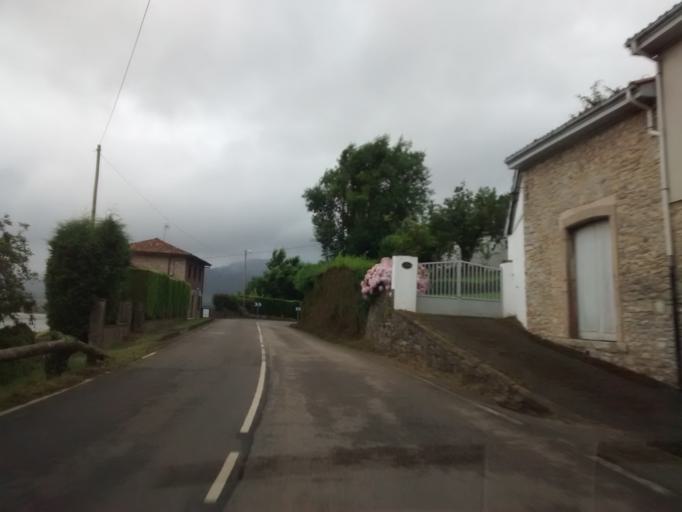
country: ES
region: Asturias
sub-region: Province of Asturias
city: Villaviciosa
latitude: 43.5197
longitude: -5.4015
